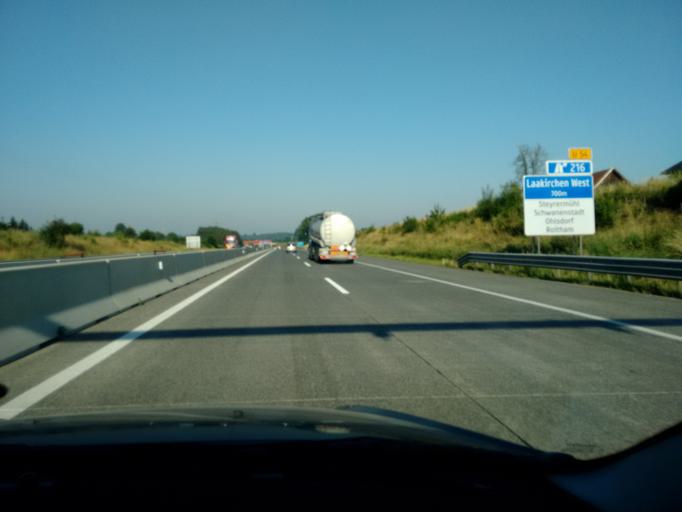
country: AT
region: Upper Austria
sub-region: Politischer Bezirk Gmunden
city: Laakirchen
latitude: 48.0024
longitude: 13.8154
